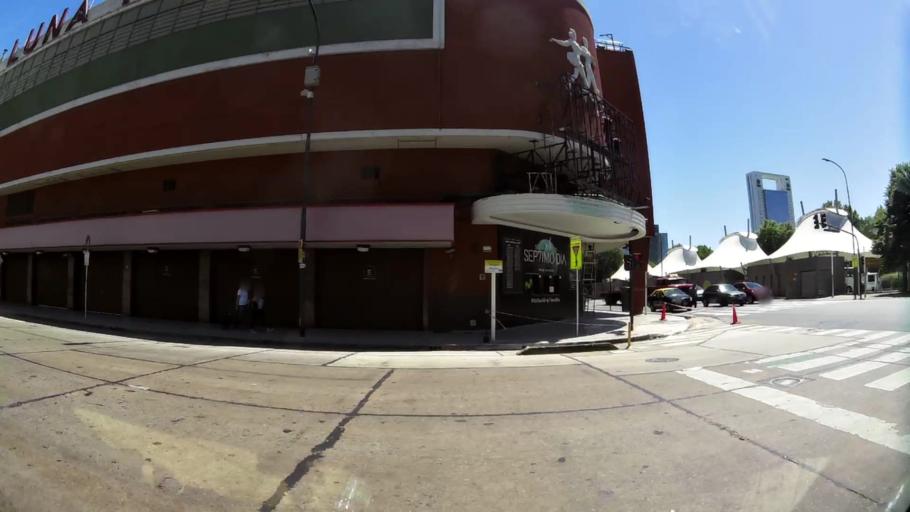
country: AR
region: Buenos Aires F.D.
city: Buenos Aires
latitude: -34.6028
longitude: -58.3684
